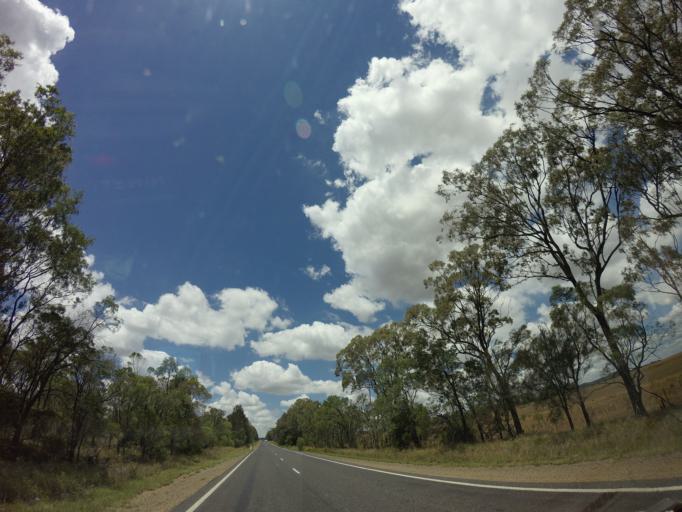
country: AU
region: Queensland
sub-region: Toowoomba
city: Oakey
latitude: -27.9482
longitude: 151.1454
